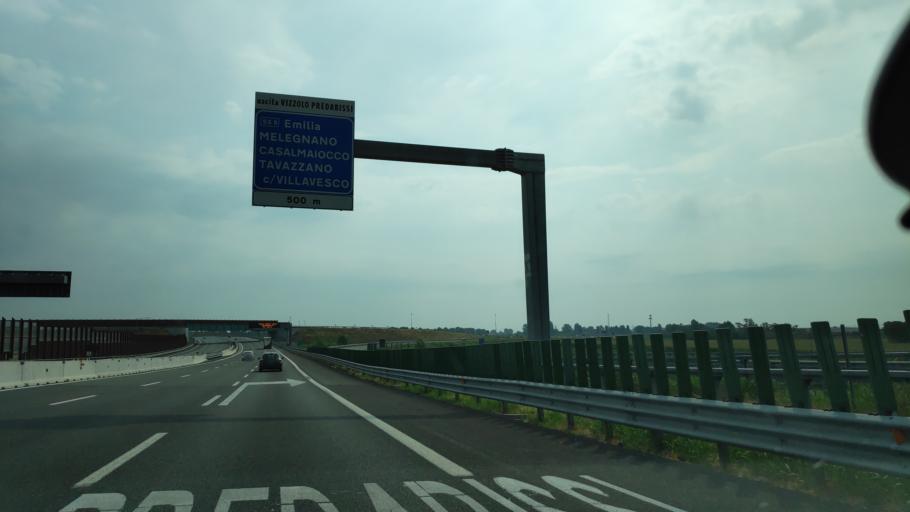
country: IT
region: Lombardy
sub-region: Citta metropolitana di Milano
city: Vizzolo Predabissi
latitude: 45.3470
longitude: 9.3416
